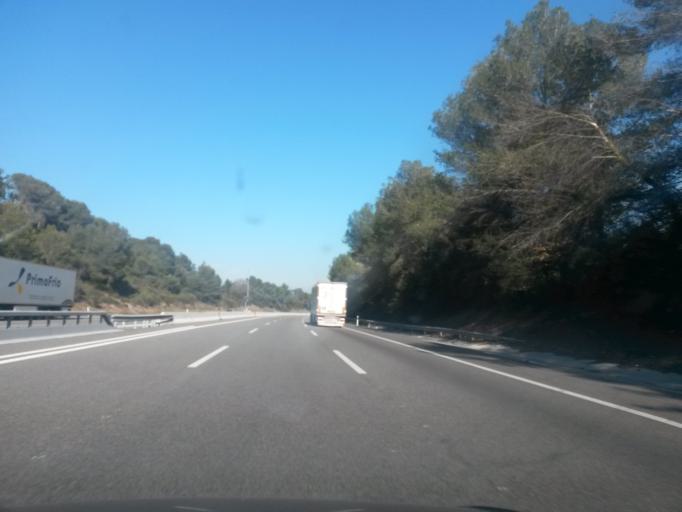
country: ES
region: Catalonia
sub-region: Provincia de Girona
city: Cervia de Ter
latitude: 42.0950
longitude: 2.8957
